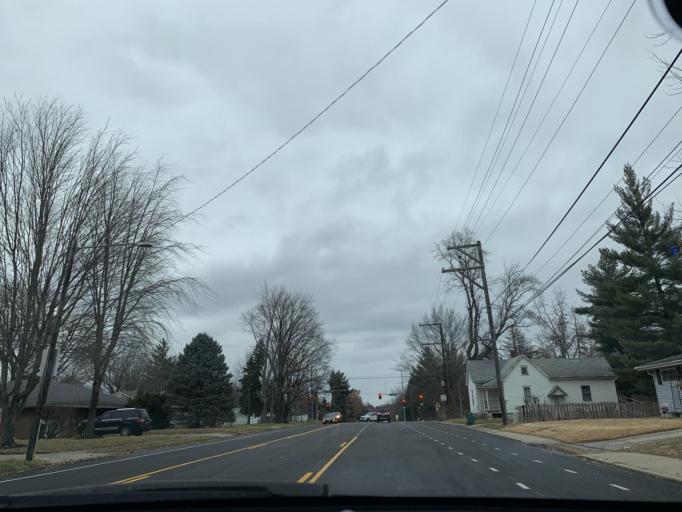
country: US
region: Illinois
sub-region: Sangamon County
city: Leland Grove
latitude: 39.8152
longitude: -89.6872
